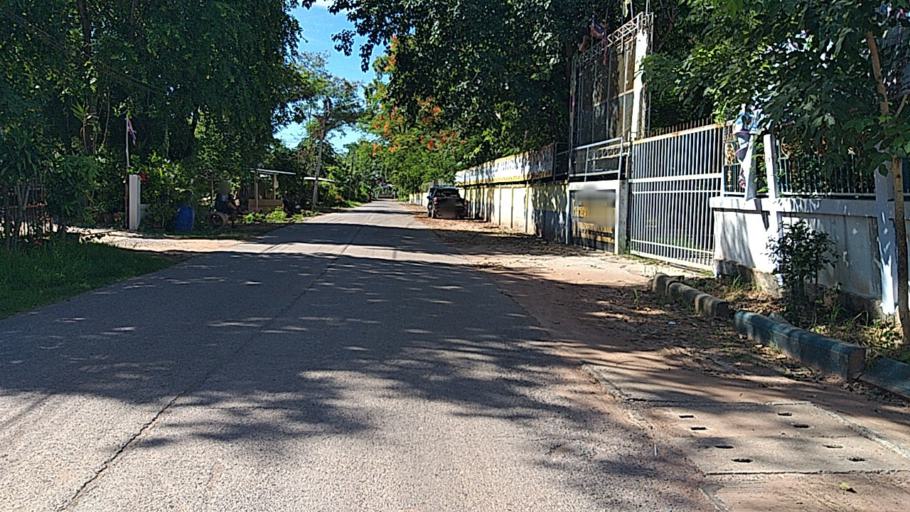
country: TH
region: Chaiyaphum
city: Ban Thaen
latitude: 16.4063
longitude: 102.3516
